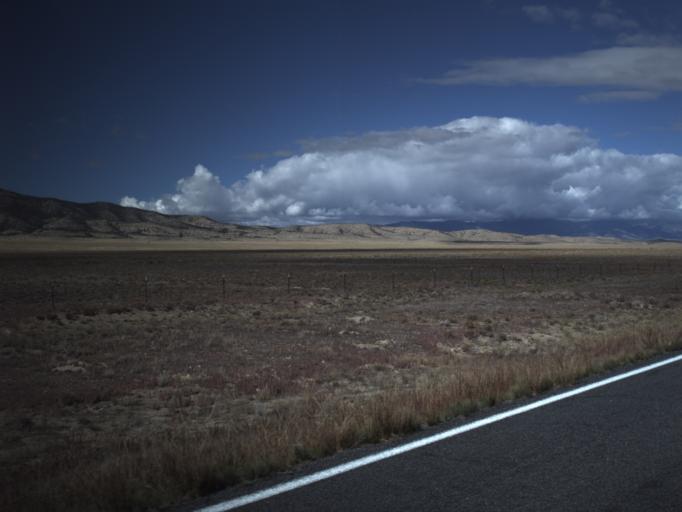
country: US
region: Utah
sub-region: Beaver County
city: Milford
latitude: 38.6513
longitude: -113.8697
